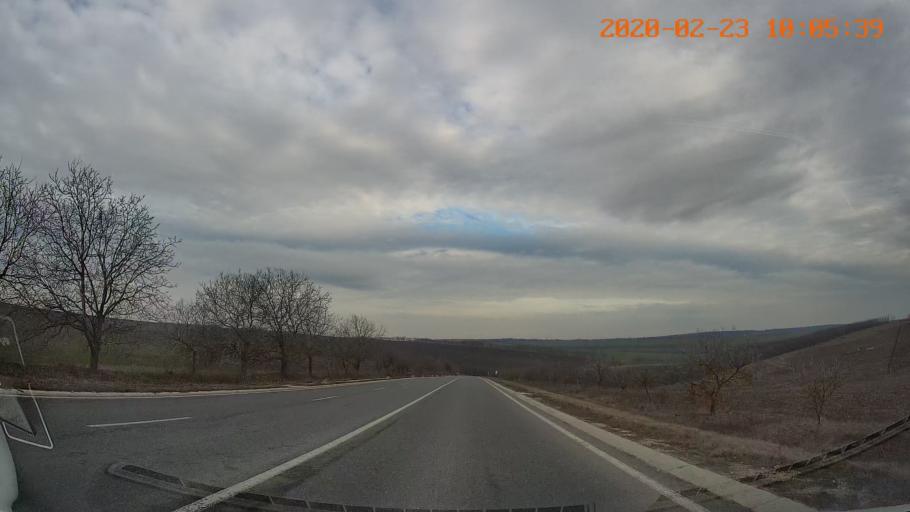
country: MD
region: Soldanesti
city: Soldanesti
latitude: 47.6932
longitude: 28.8360
